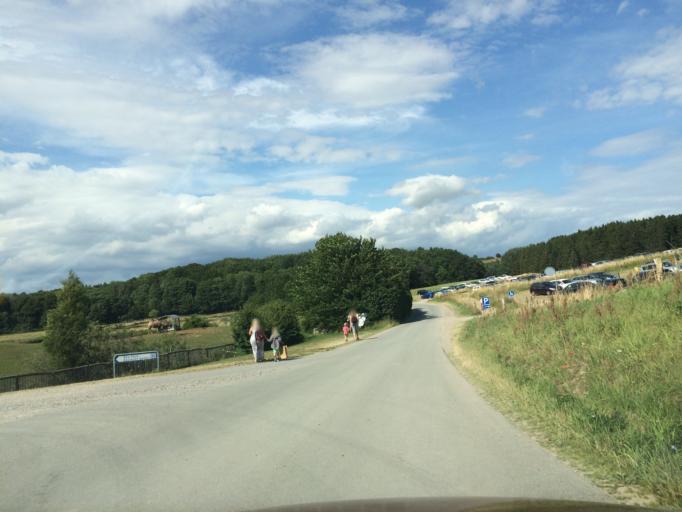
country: DK
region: Central Jutland
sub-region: Syddjurs Kommune
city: Ebeltoft
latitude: 56.2636
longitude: 10.7419
